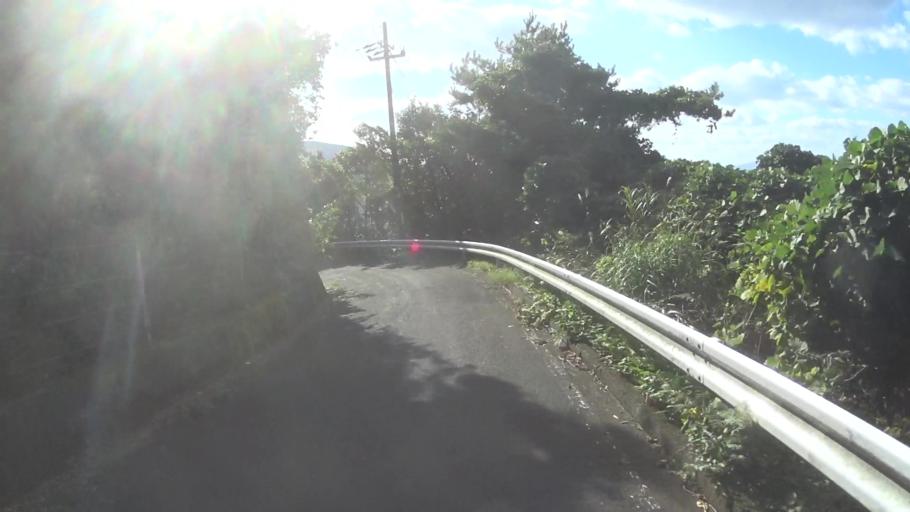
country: JP
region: Kyoto
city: Maizuru
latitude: 35.5678
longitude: 135.4122
